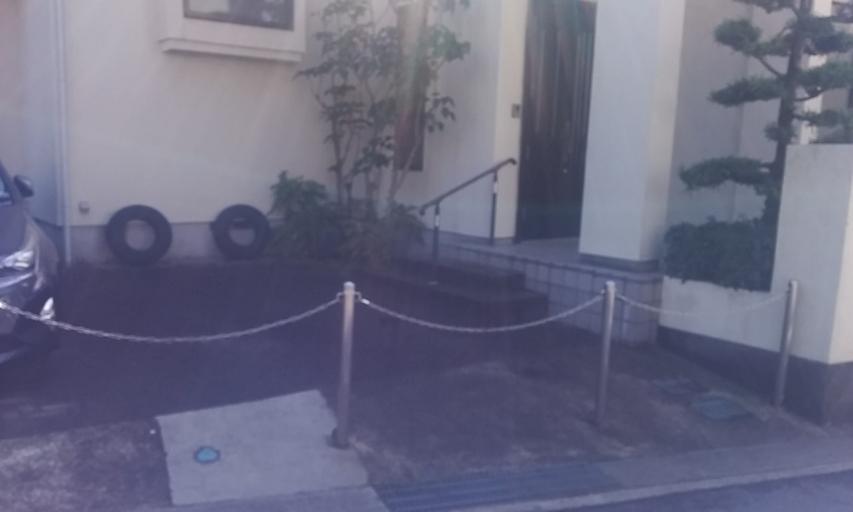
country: JP
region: Kanagawa
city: Kamakura
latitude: 35.3204
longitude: 139.5385
